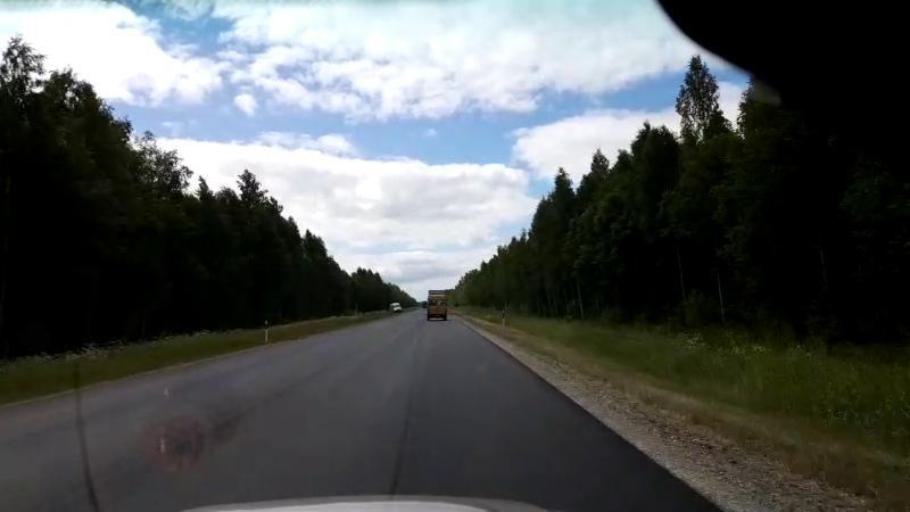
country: LV
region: Salacgrivas
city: Ainazi
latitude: 57.9308
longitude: 24.4267
